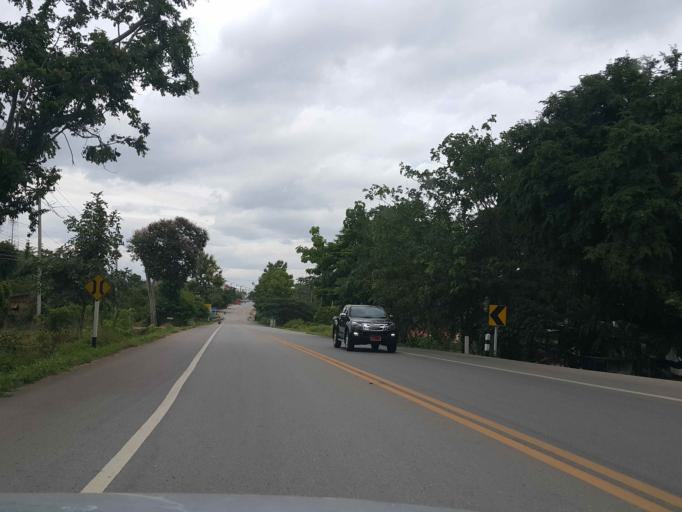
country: TH
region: Lamphun
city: Li
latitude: 17.7949
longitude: 98.9528
